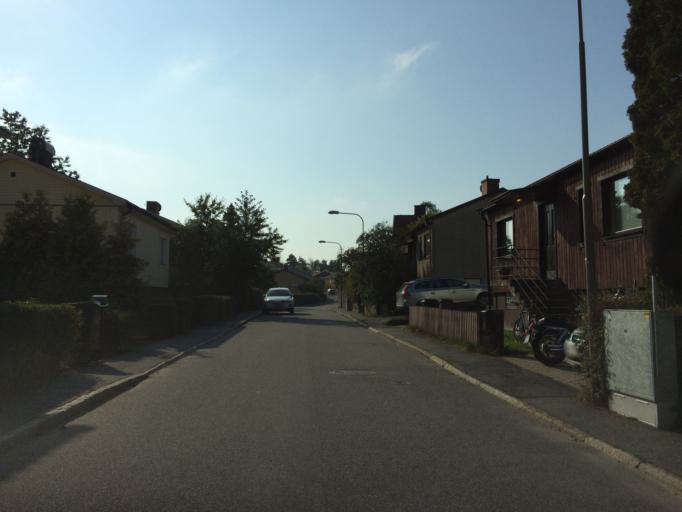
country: SE
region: Stockholm
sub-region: Huddinge Kommun
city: Huddinge
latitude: 59.2942
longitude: 17.9927
